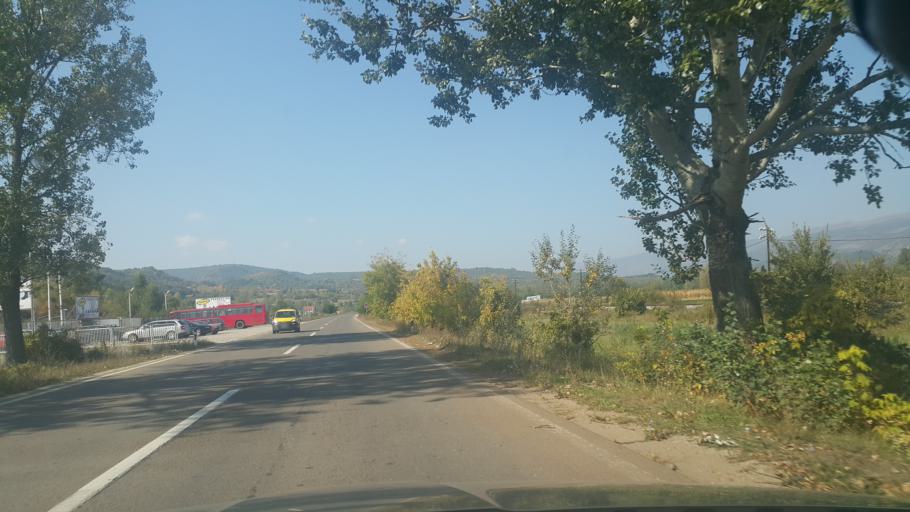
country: RS
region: Central Serbia
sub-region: Pirotski Okrug
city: Bela Palanka
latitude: 43.2308
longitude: 22.2809
